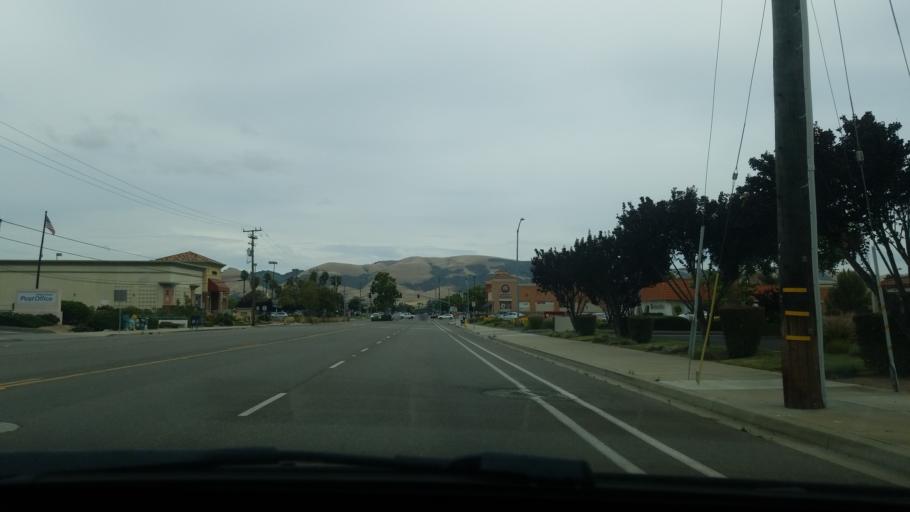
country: US
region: California
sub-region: San Luis Obispo County
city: Nipomo
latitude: 35.0346
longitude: -120.4885
